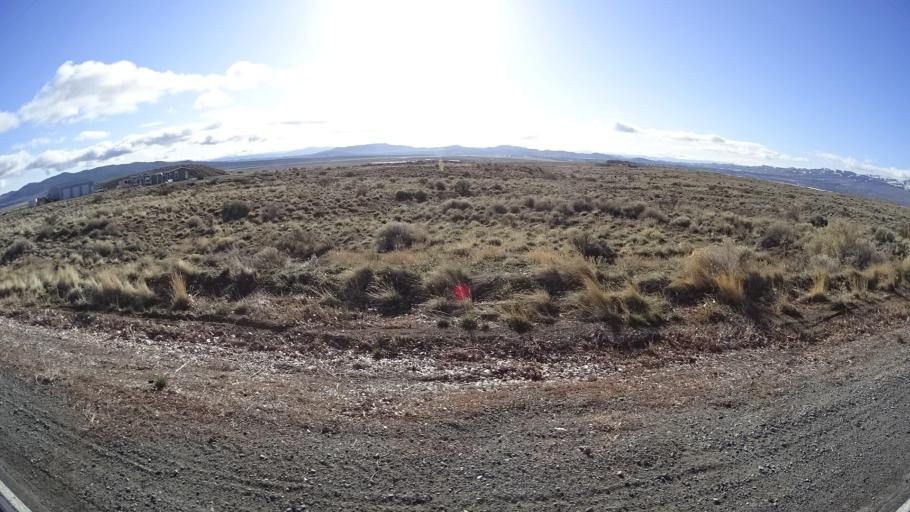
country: US
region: Nevada
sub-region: Washoe County
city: Cold Springs
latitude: 39.6840
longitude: -119.9204
